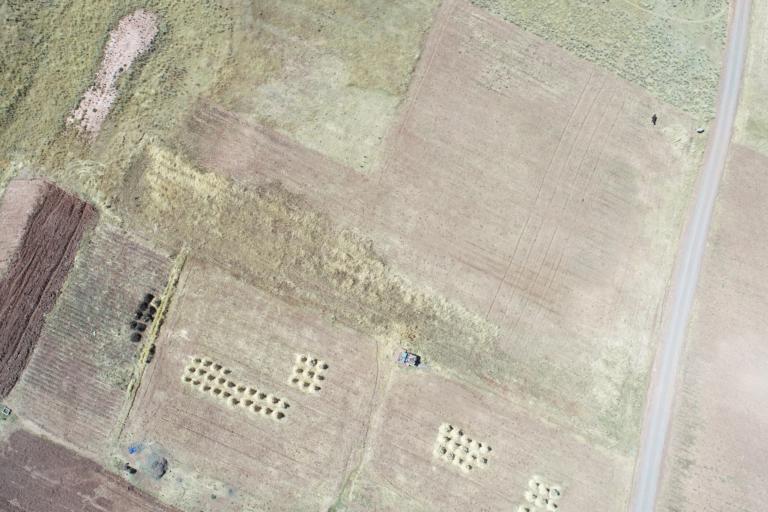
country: BO
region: La Paz
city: Tiahuanaco
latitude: -16.5938
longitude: -68.7712
